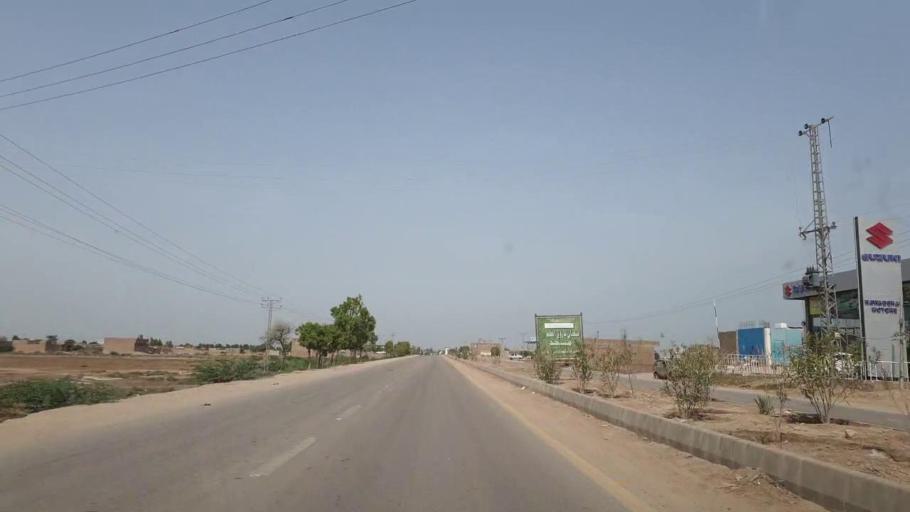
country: PK
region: Sindh
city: Nawabshah
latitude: 26.2279
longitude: 68.3636
